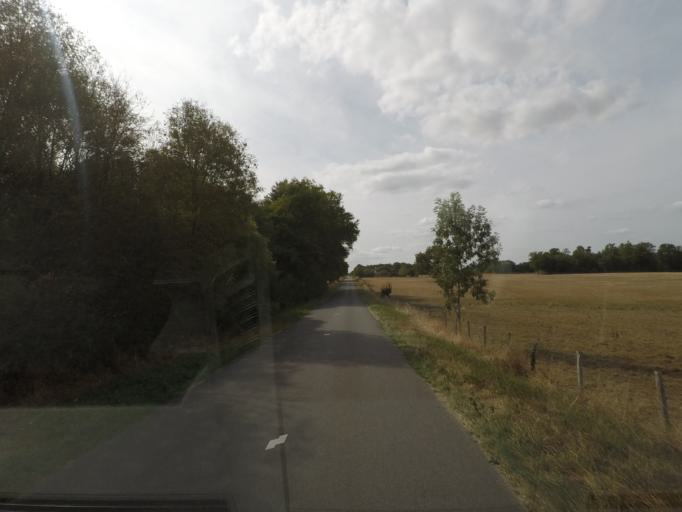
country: FR
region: Poitou-Charentes
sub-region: Departement de la Charente
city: Loubert
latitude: 45.9419
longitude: 0.5209
